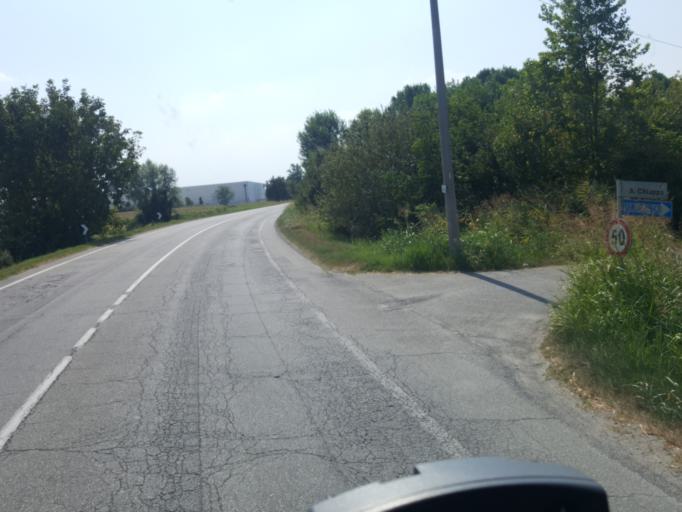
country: IT
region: Emilia-Romagna
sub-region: Provincia di Piacenza
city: Monticelli d'Ongina
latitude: 45.0764
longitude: 9.9051
